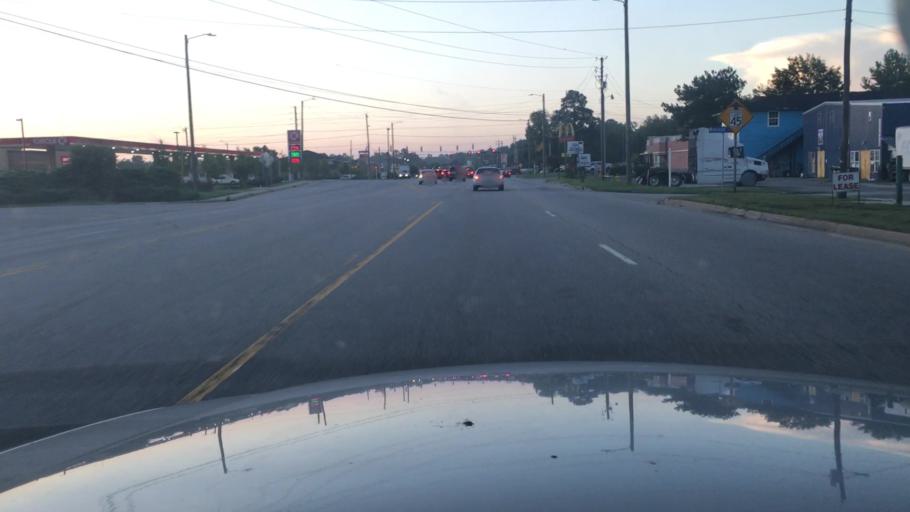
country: US
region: North Carolina
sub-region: Cumberland County
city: Fort Bragg
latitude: 35.0623
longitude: -79.0173
